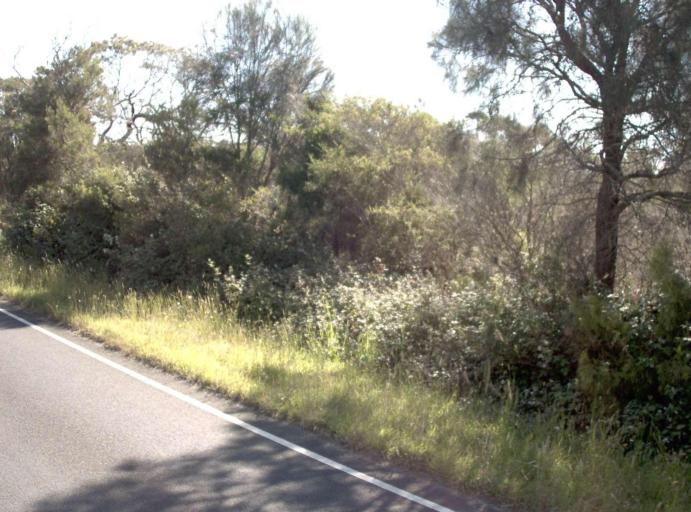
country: AU
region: Victoria
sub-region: Latrobe
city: Traralgon
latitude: -38.6376
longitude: 146.6734
